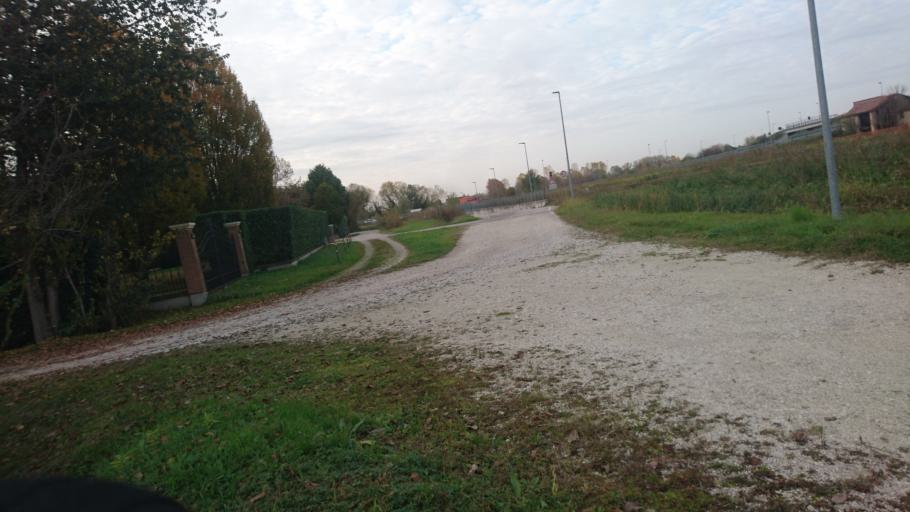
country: IT
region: Veneto
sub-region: Provincia di Padova
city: Tencarola
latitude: 45.3791
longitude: 11.8275
